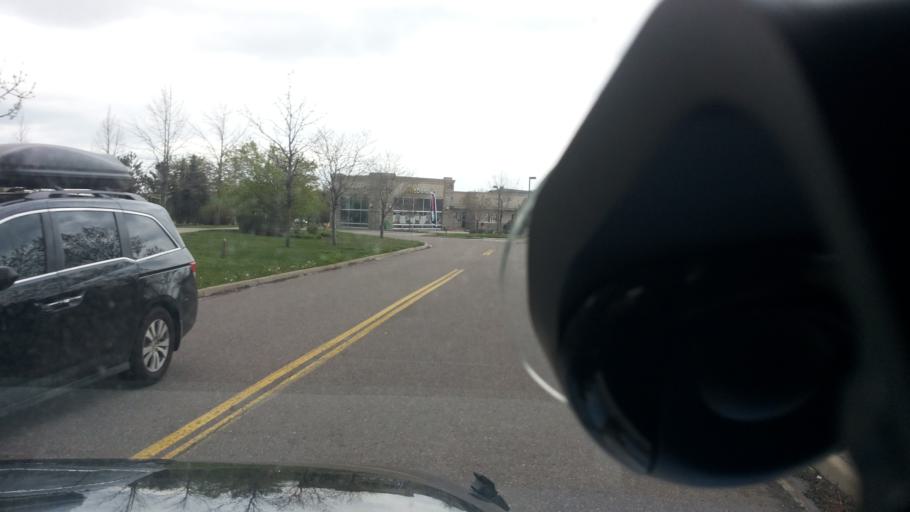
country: US
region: Colorado
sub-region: Boulder County
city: Superior
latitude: 39.9624
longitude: -105.1629
